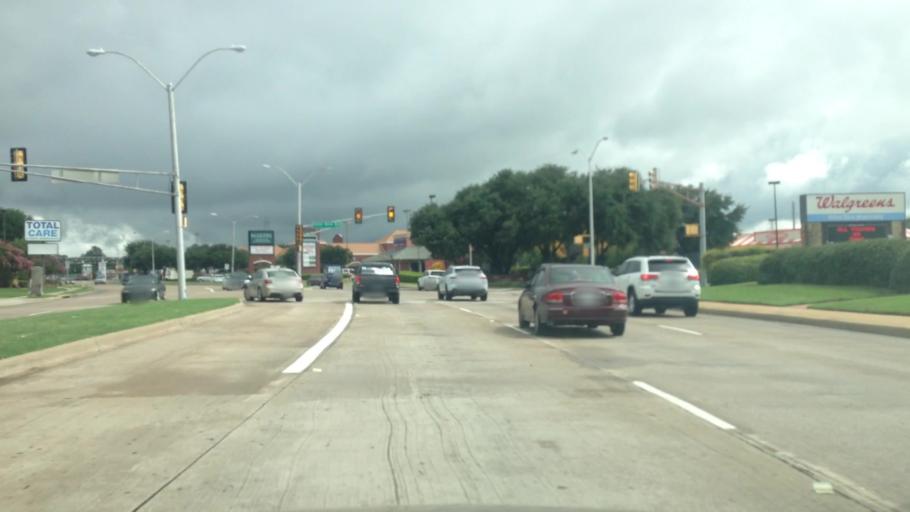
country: US
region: Texas
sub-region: Tarrant County
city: Benbrook
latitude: 32.6619
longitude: -97.4023
